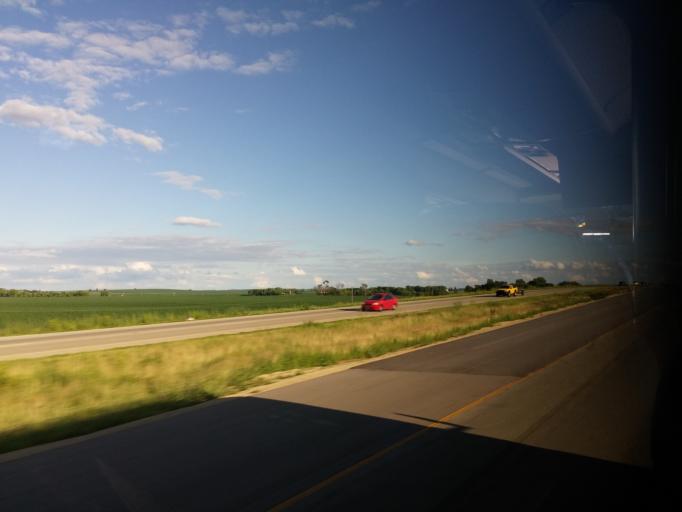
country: US
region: Wisconsin
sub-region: Rock County
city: Janesville
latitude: 42.6257
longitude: -88.9829
